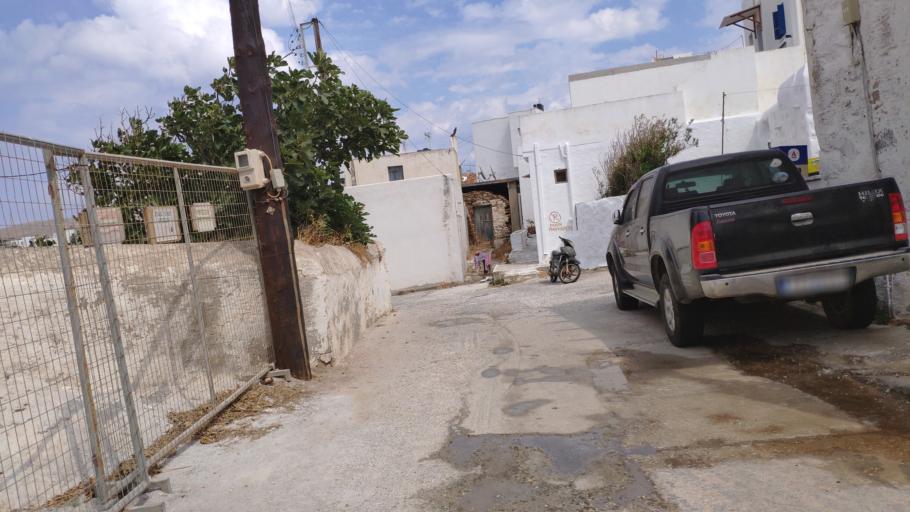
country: GR
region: South Aegean
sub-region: Nomos Kykladon
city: Kythnos
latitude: 37.4130
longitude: 24.4303
